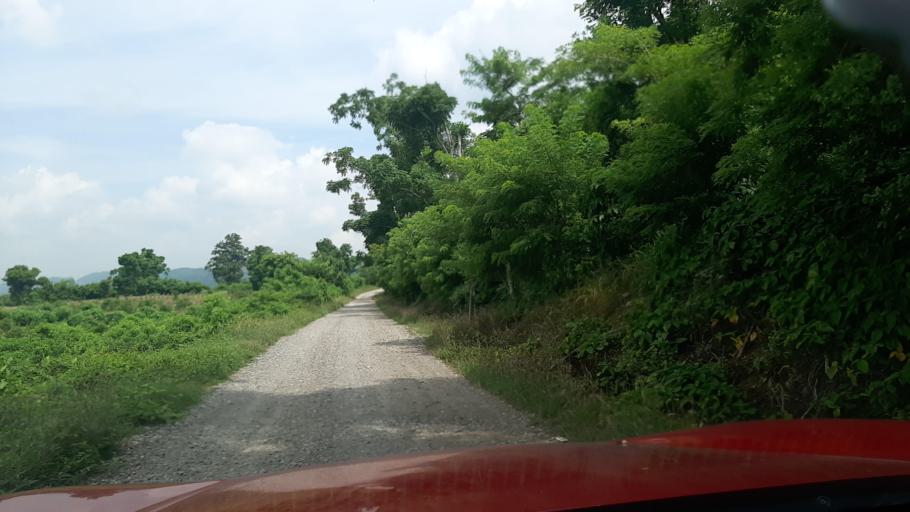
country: MX
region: Veracruz
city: Gutierrez Zamora
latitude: 20.4560
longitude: -97.1778
